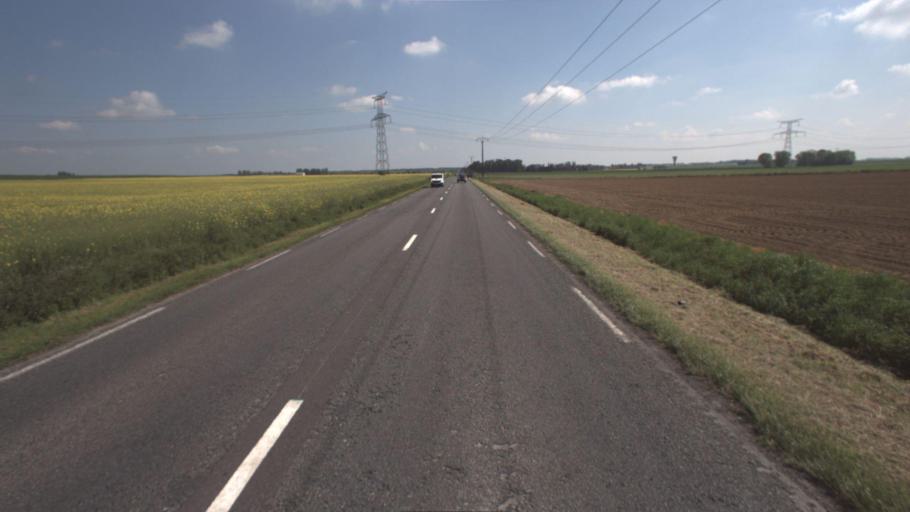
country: FR
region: Ile-de-France
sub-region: Departement de Seine-et-Marne
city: Guignes
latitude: 48.6259
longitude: 2.7698
